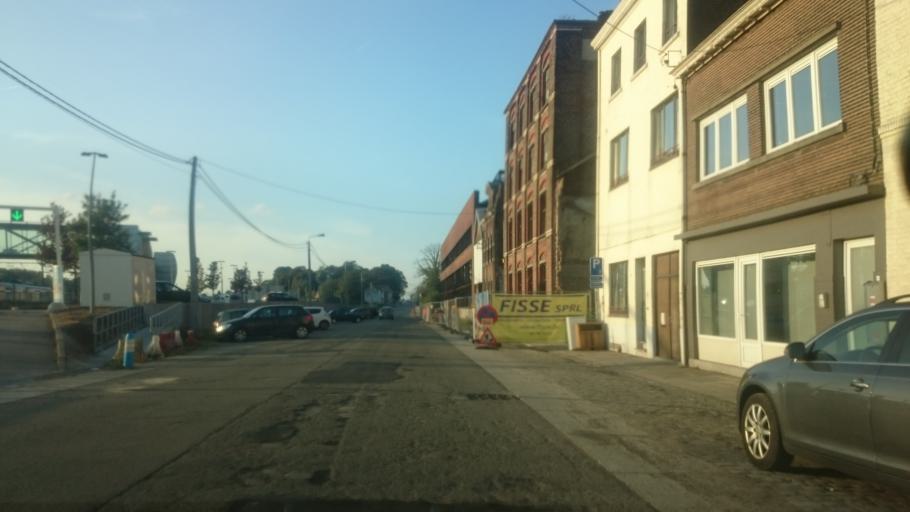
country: BE
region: Wallonia
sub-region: Province de Namur
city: Gembloux
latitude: 50.5698
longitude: 4.6929
